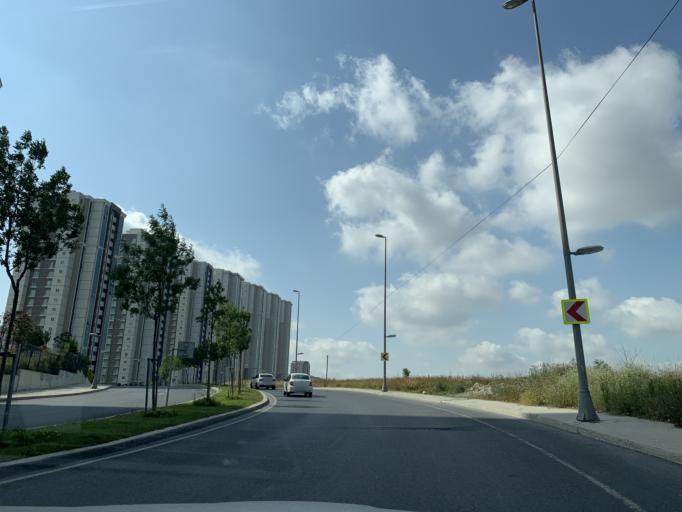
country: TR
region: Istanbul
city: Esenyurt
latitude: 41.0759
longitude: 28.6987
